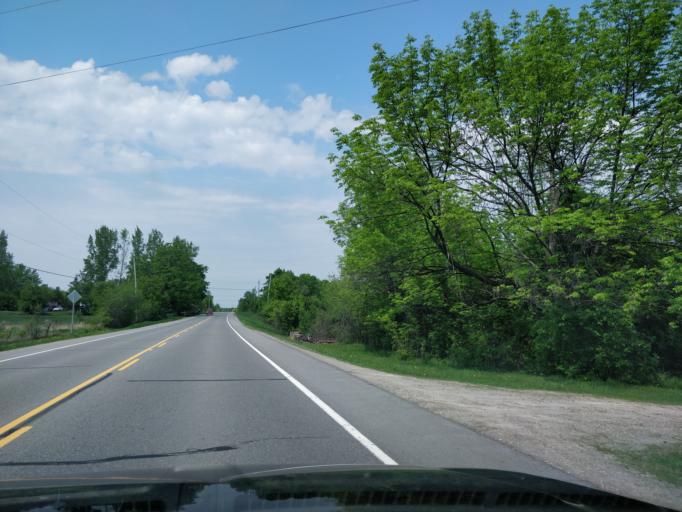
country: CA
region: Ontario
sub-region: Lanark County
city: Smiths Falls
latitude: 45.0136
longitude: -76.0798
